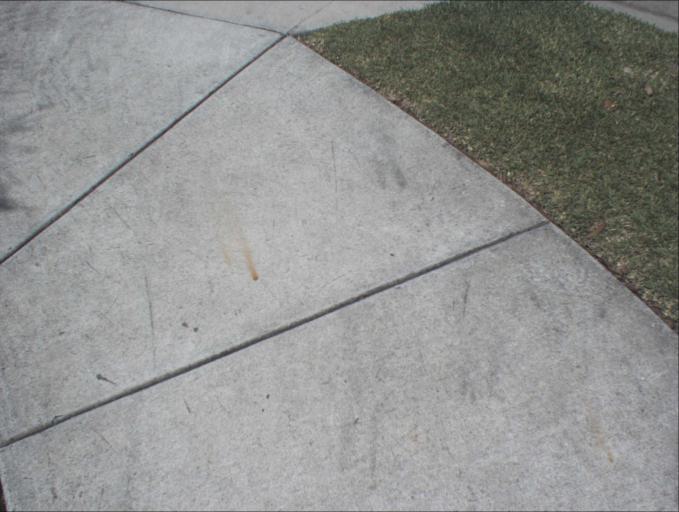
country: AU
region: Queensland
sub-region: Logan
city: Waterford West
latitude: -27.7138
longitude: 153.1445
